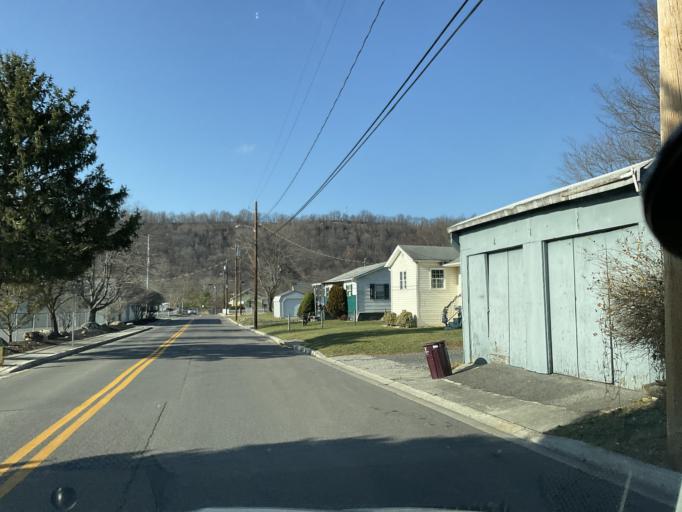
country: US
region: West Virginia
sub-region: Mineral County
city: Wiley Ford
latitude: 39.6289
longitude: -78.7688
